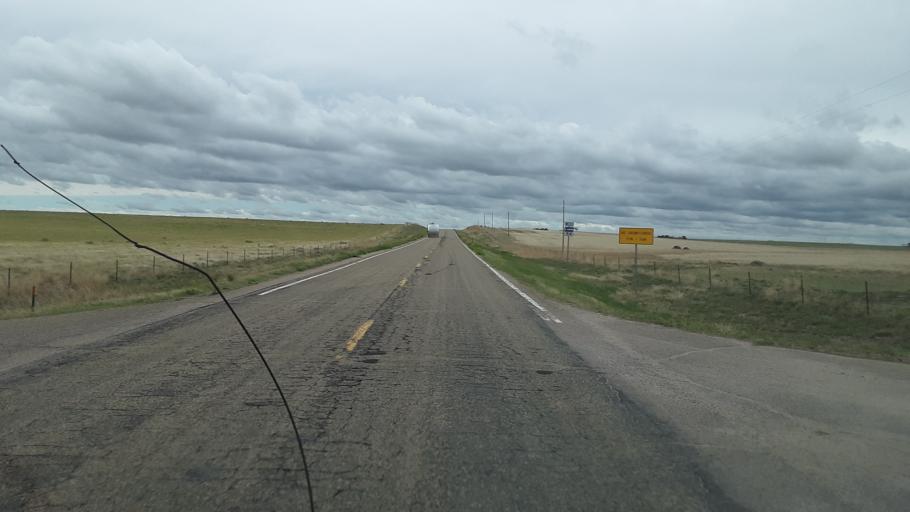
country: US
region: Colorado
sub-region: Lincoln County
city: Limon
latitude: 38.8384
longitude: -103.8696
